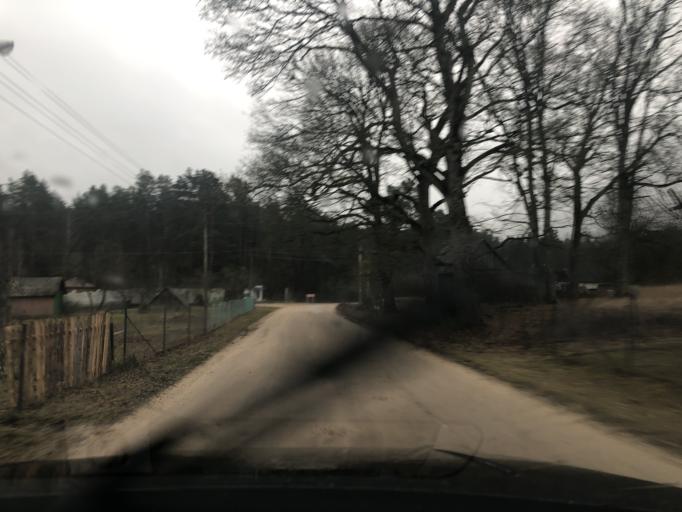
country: BY
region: Grodnenskaya
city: Skidal'
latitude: 53.8573
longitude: 24.2513
